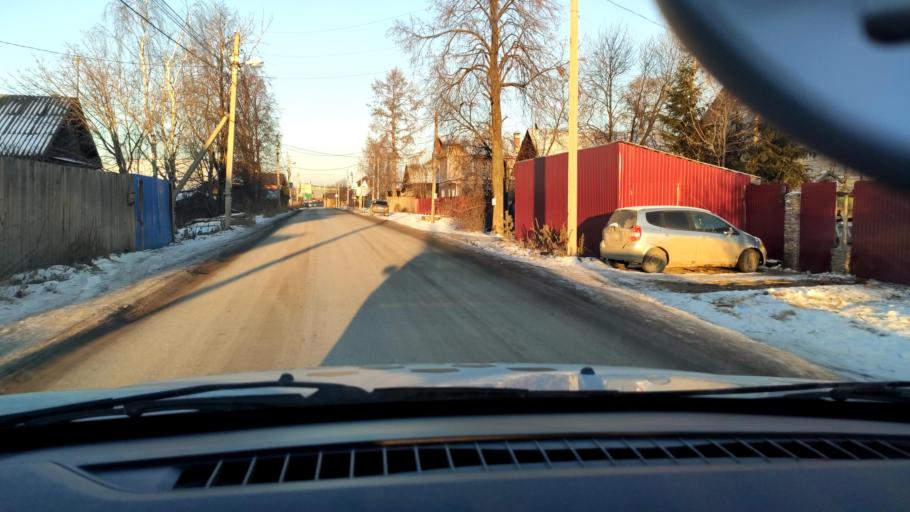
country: RU
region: Perm
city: Ferma
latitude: 57.9033
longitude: 56.3040
